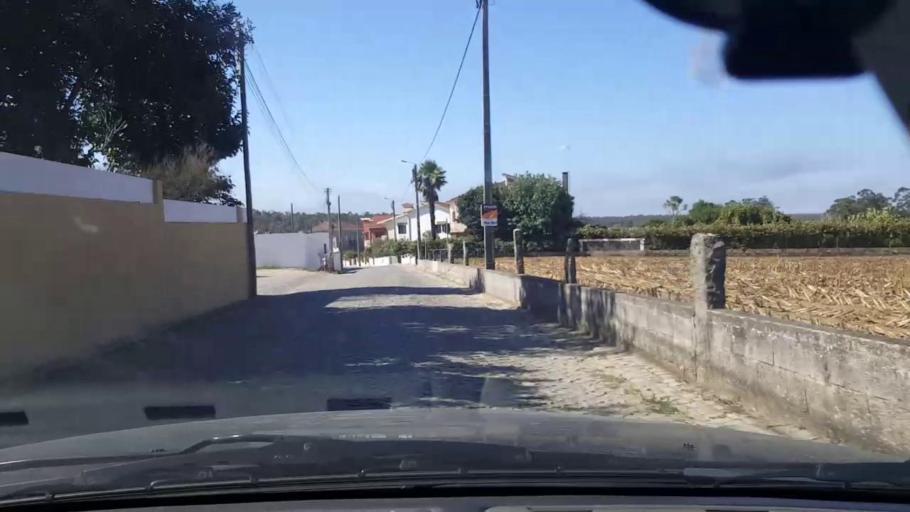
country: PT
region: Porto
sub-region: Maia
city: Gemunde
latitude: 41.2820
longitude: -8.6582
